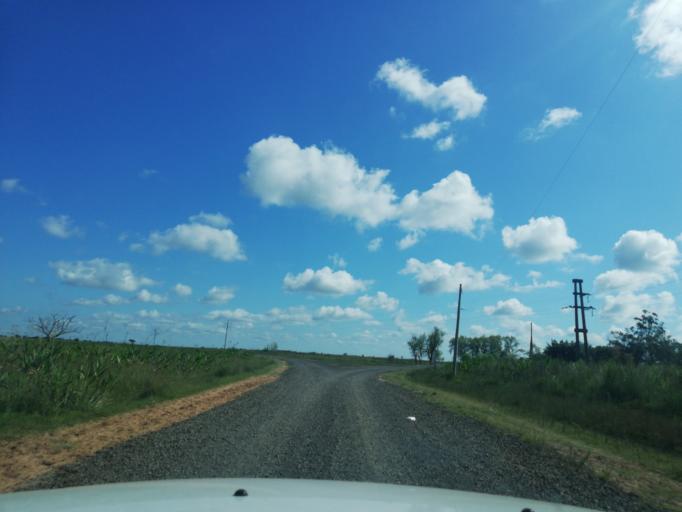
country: AR
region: Corrientes
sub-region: Departamento de San Miguel
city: San Miguel
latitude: -27.9825
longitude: -57.5813
